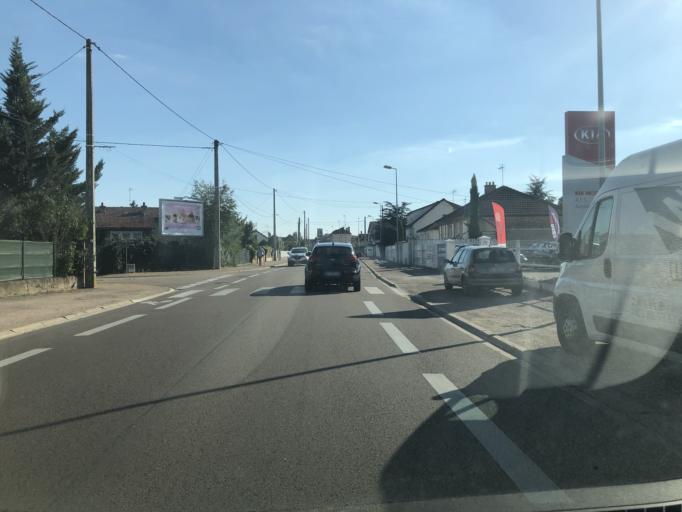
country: FR
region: Bourgogne
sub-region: Departement de l'Yonne
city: Auxerre
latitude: 47.8060
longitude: 3.5800
